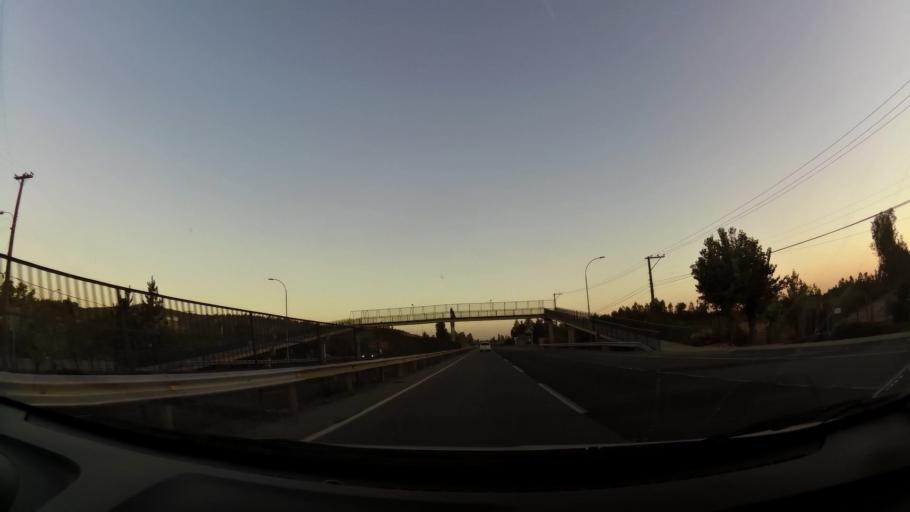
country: CL
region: Maule
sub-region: Provincia de Linares
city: Linares
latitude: -35.7637
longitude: -71.6698
